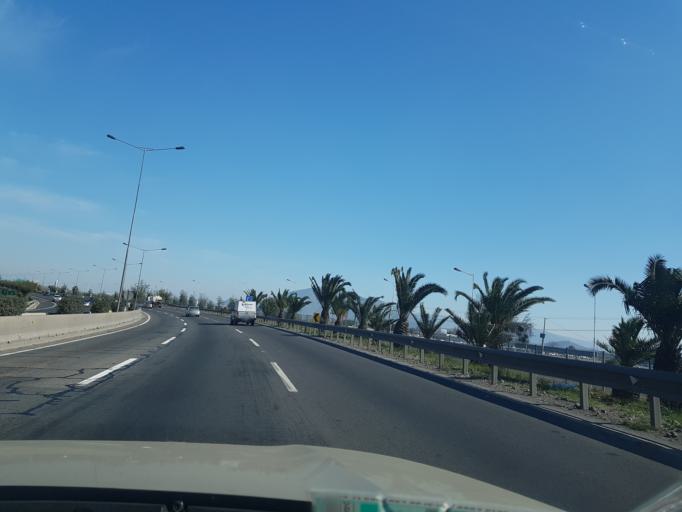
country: CL
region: Santiago Metropolitan
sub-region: Provincia de Santiago
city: Lo Prado
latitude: -33.4052
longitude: -70.7822
